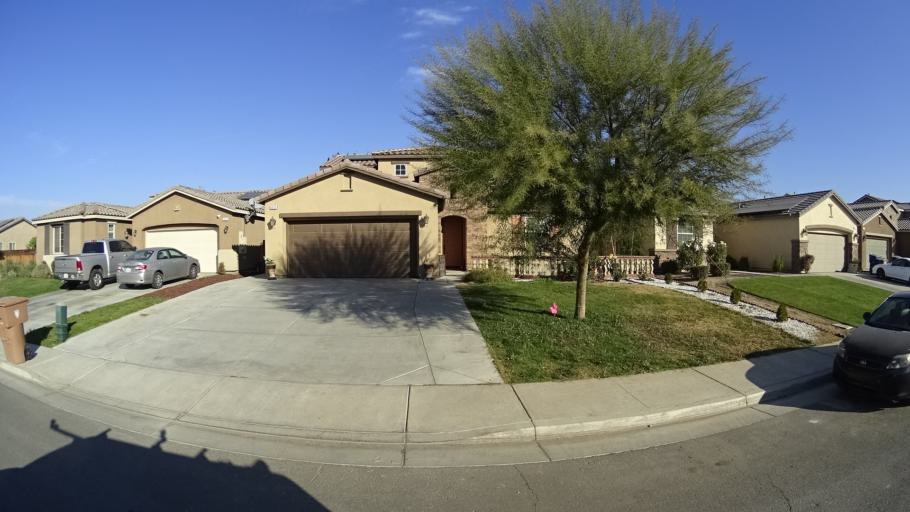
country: US
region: California
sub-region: Kern County
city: Greenfield
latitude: 35.2786
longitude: -119.0675
